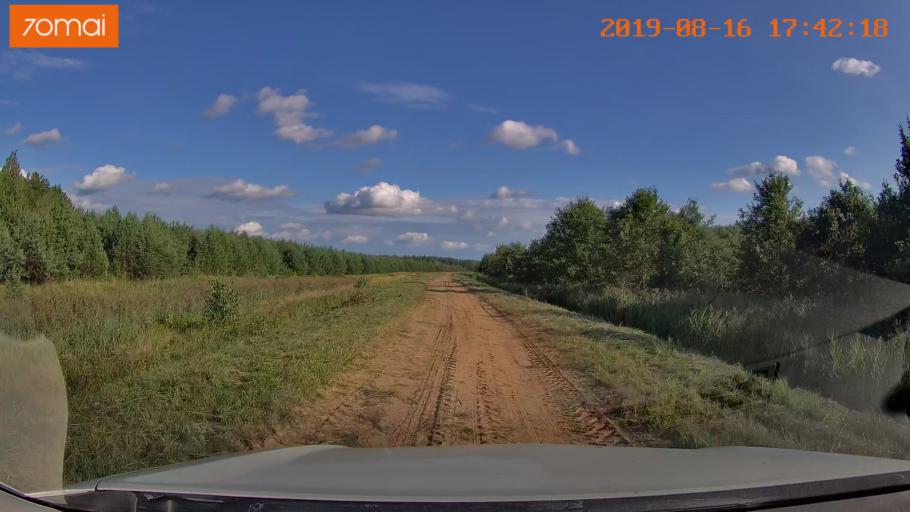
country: BY
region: Mogilev
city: Asipovichy
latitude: 53.2369
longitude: 28.6653
